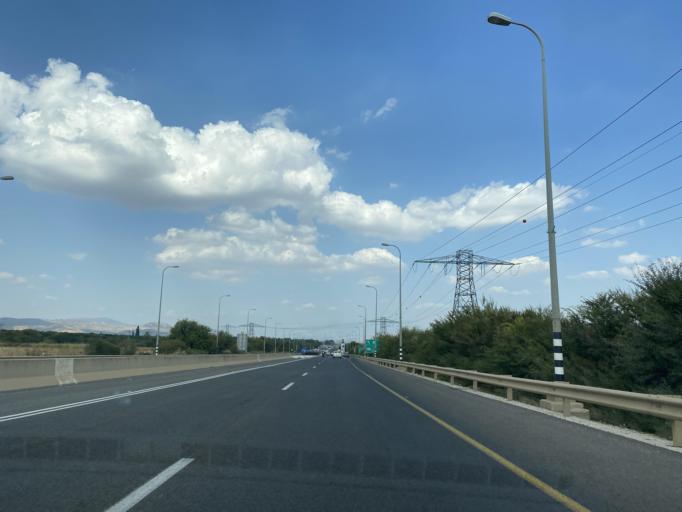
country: IL
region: Northern District
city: Rosh Pinna
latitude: 32.9864
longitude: 35.5597
